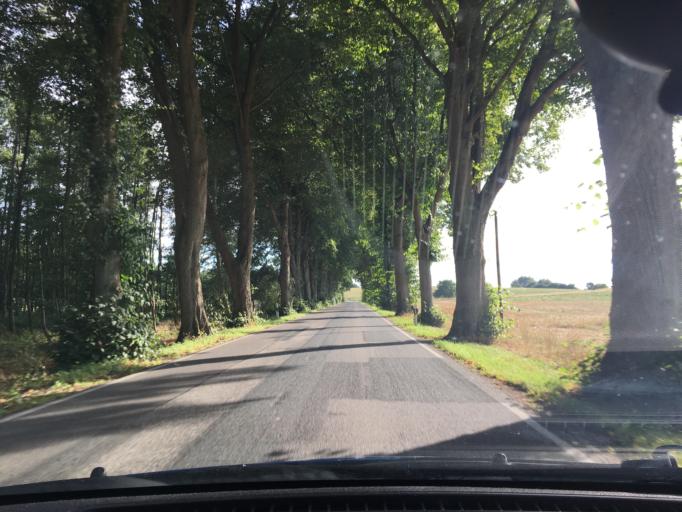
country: DE
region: Lower Saxony
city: Stelle
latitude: 53.3411
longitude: 10.0838
